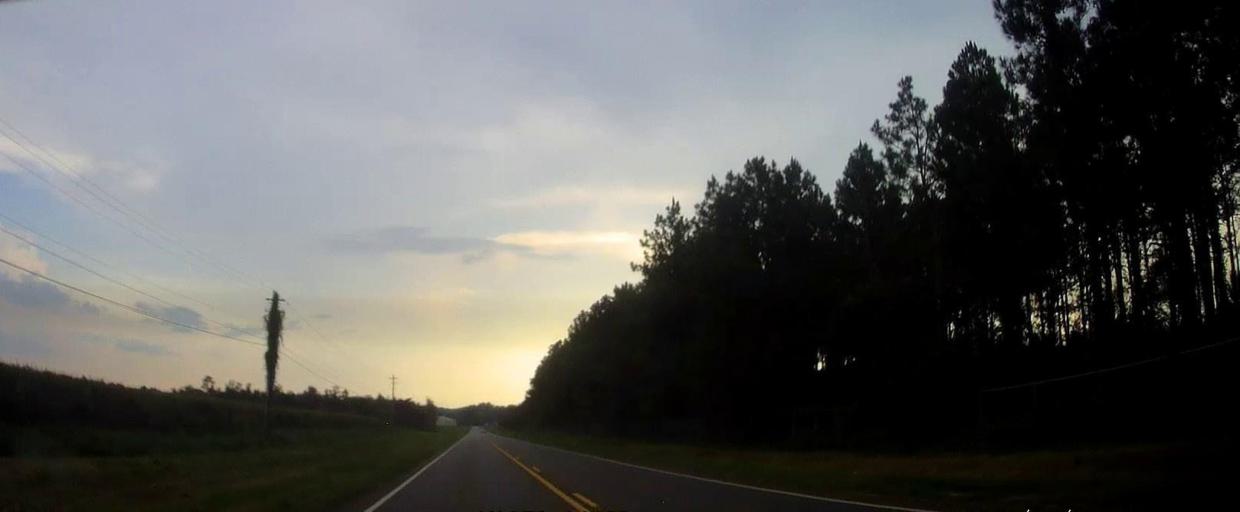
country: US
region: Georgia
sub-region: Laurens County
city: East Dublin
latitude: 32.5526
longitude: -82.8443
